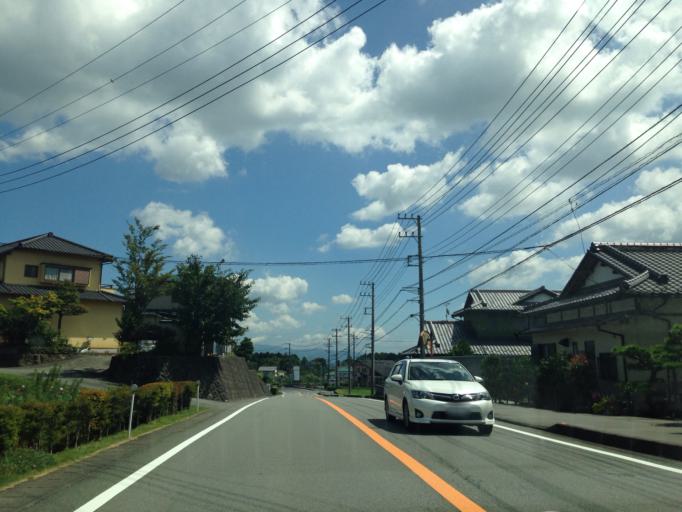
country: JP
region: Shizuoka
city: Gotemba
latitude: 35.2206
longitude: 138.8901
